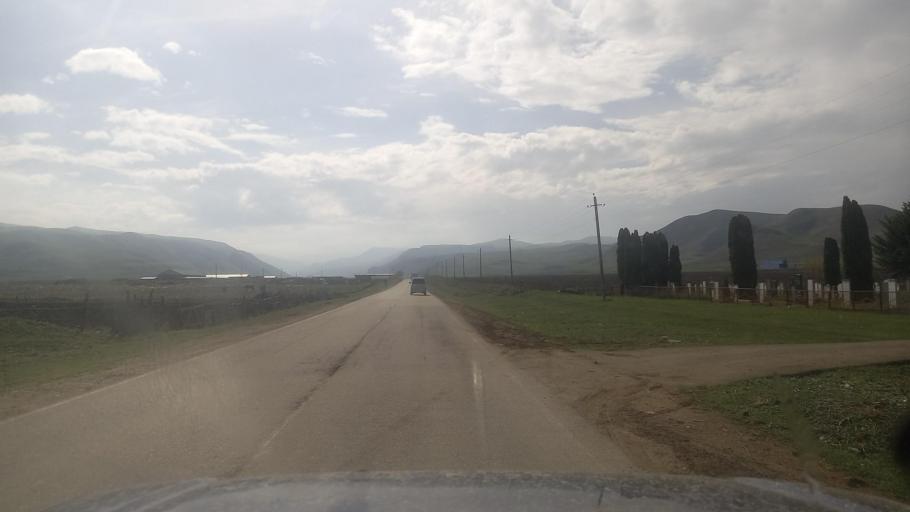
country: RU
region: Kabardino-Balkariya
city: Kamennomostskoye
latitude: 43.7361
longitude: 43.0152
